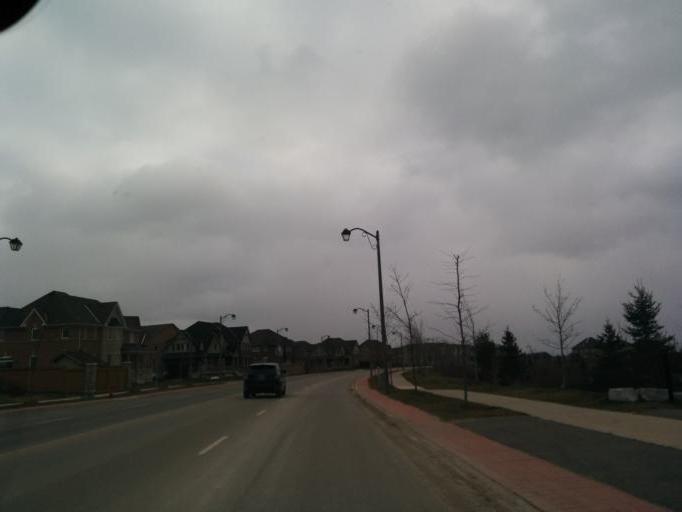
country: CA
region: Ontario
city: Brampton
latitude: 43.7544
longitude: -79.8246
